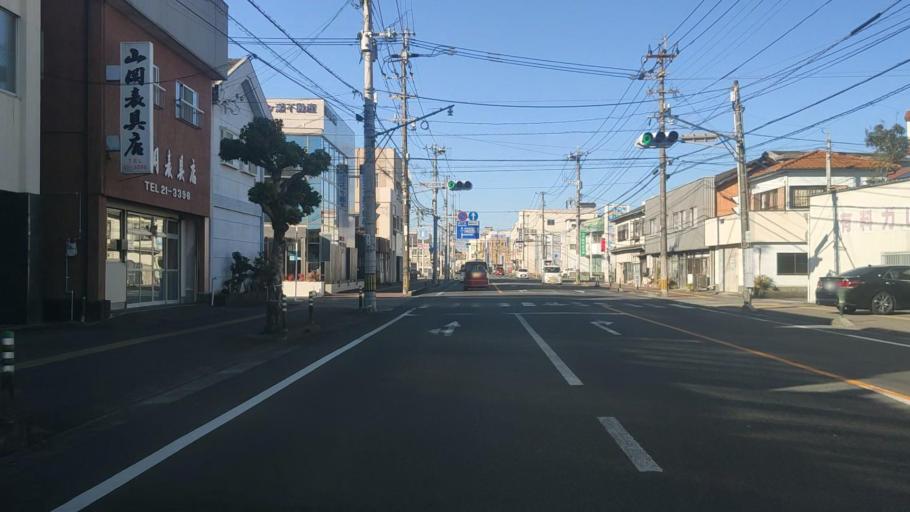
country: JP
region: Miyazaki
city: Nobeoka
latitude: 32.5853
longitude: 131.6730
